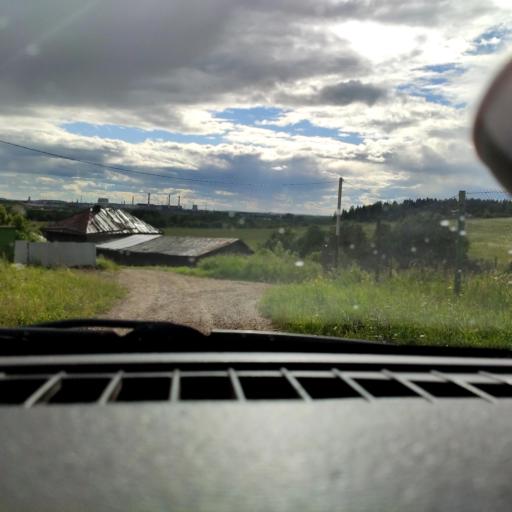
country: RU
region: Perm
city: Froly
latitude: 57.9356
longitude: 56.2083
